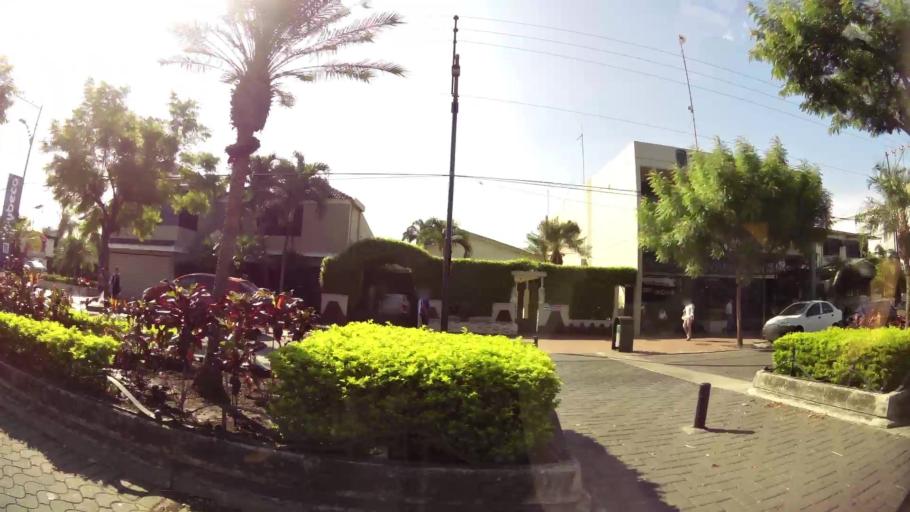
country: EC
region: Guayas
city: Guayaquil
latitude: -2.1730
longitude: -79.9063
